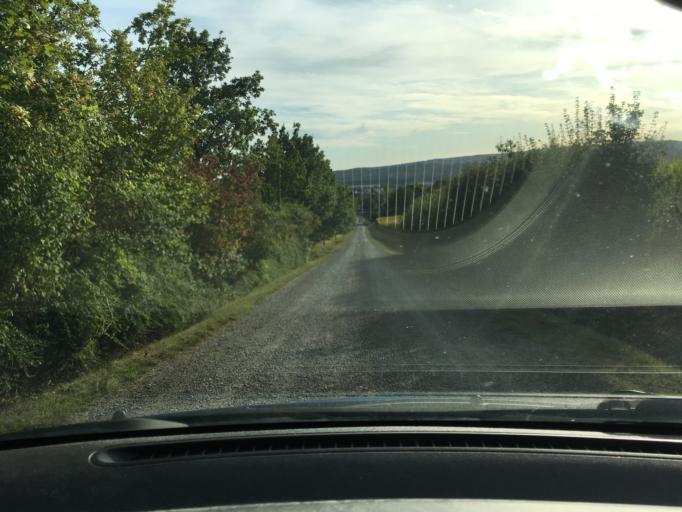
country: DE
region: Lower Saxony
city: Bad Munder am Deister
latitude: 52.2040
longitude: 9.4767
